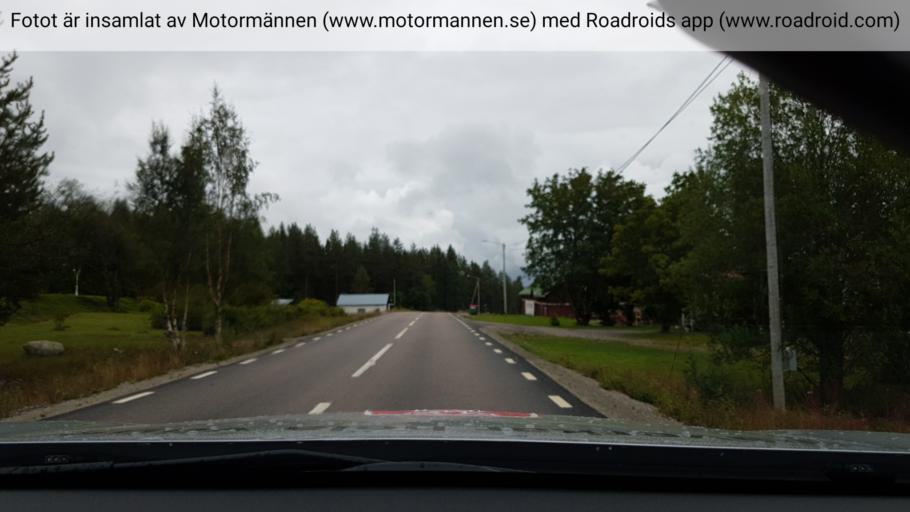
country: SE
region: Vaesterbotten
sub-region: Lycksele Kommun
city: Soderfors
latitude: 64.7101
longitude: 17.7087
